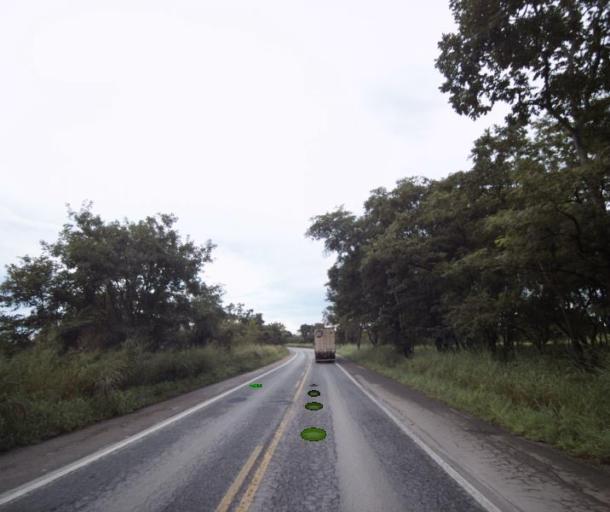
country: BR
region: Goias
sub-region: Porangatu
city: Porangatu
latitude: -13.6491
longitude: -49.0391
